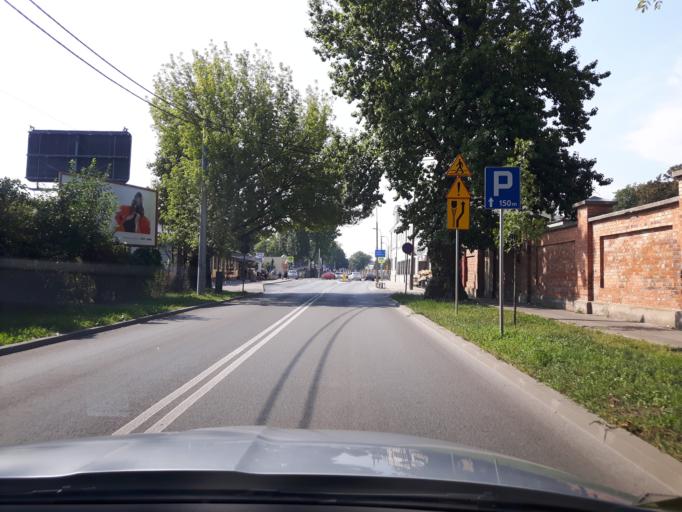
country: PL
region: Masovian Voivodeship
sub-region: Warszawa
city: Targowek
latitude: 52.2792
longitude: 21.0451
